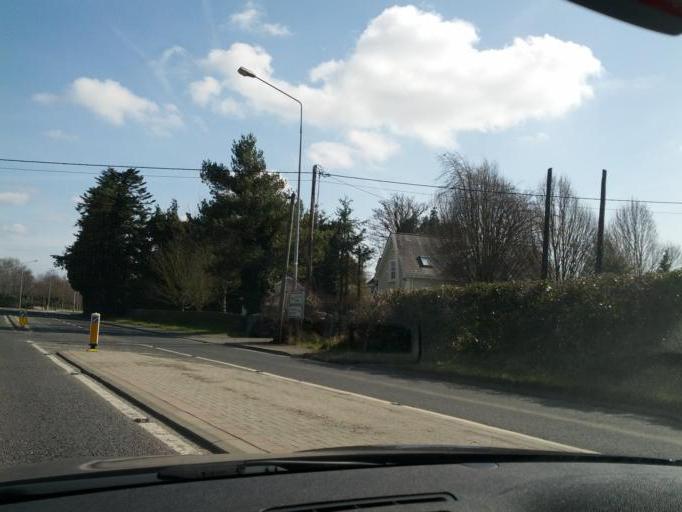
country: IE
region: Leinster
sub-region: Kildare
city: Leixlip
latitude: 53.3747
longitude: -6.5306
